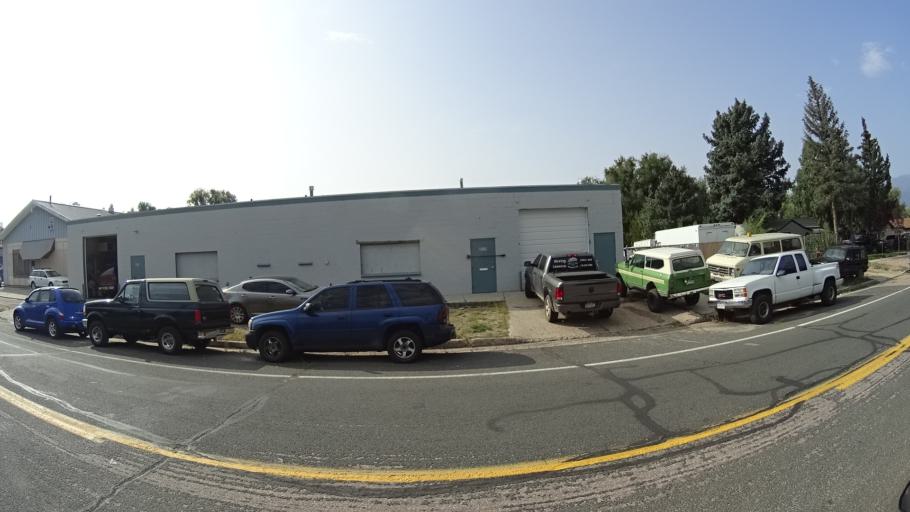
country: US
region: Colorado
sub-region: El Paso County
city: Colorado Springs
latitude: 38.8409
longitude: -104.7812
